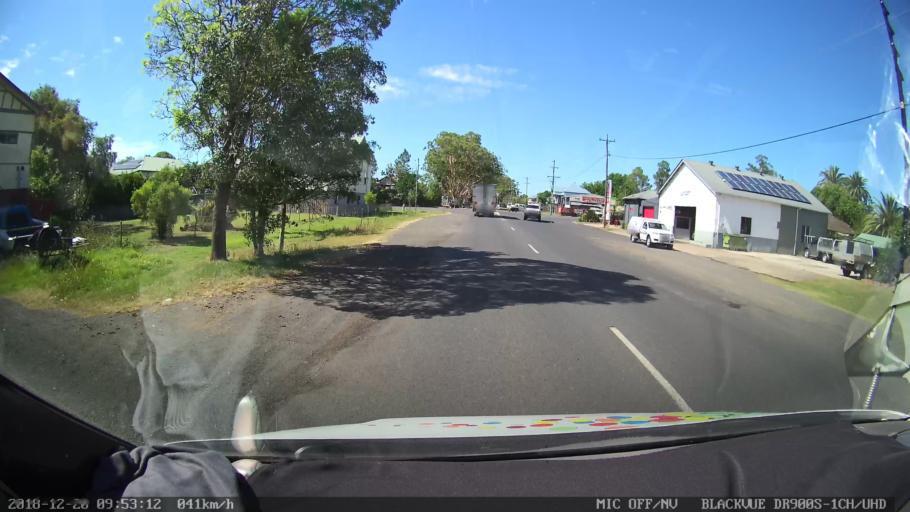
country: AU
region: New South Wales
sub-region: Lismore Municipality
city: Lismore
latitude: -28.8010
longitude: 153.2699
